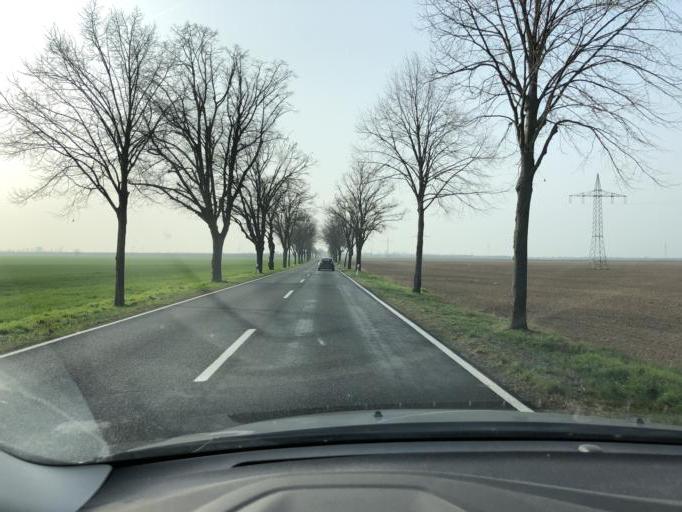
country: DE
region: Saxony-Anhalt
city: Roitzsch
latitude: 51.5468
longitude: 12.2469
